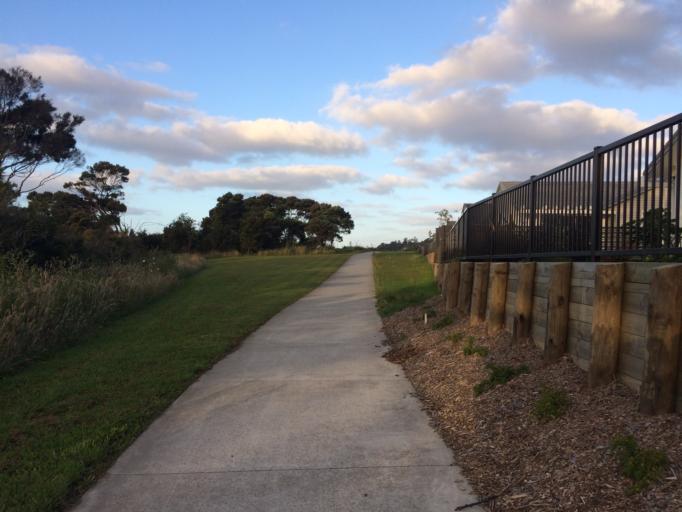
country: NZ
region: Auckland
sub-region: Auckland
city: Rosebank
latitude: -36.7896
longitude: 174.6584
